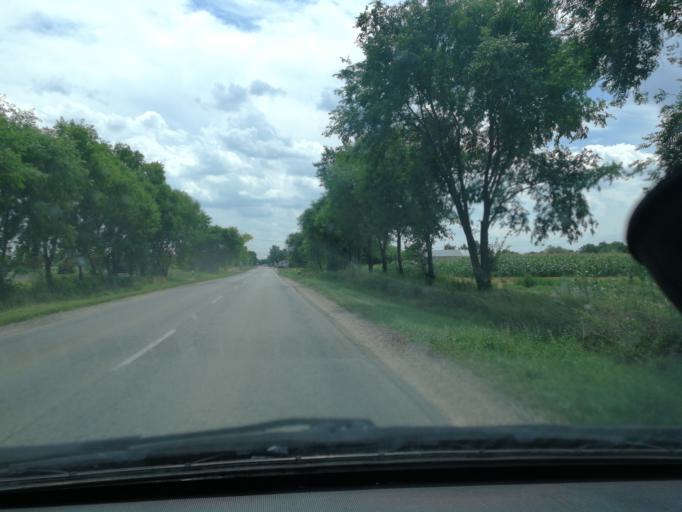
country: HU
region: Bacs-Kiskun
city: Solt
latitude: 46.8132
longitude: 19.0057
